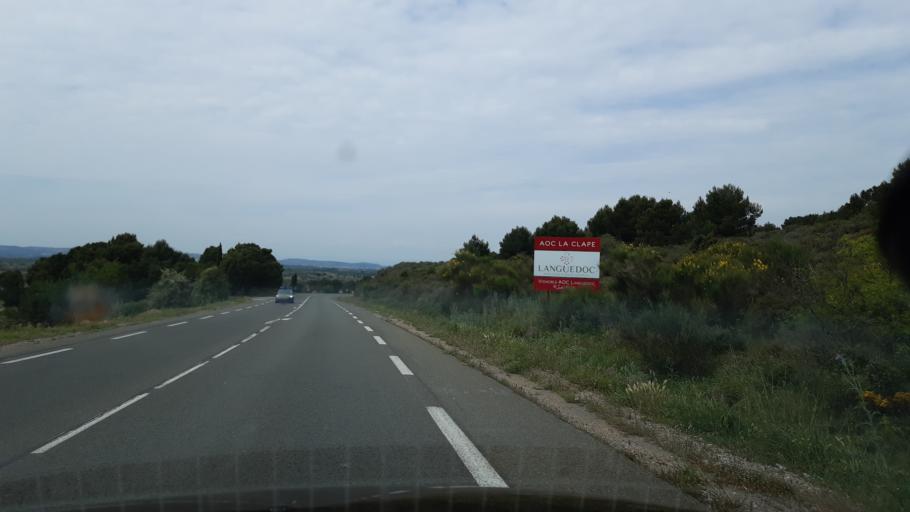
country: FR
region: Languedoc-Roussillon
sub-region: Departement de l'Aude
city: Gruissan
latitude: 43.1296
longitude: 3.0569
